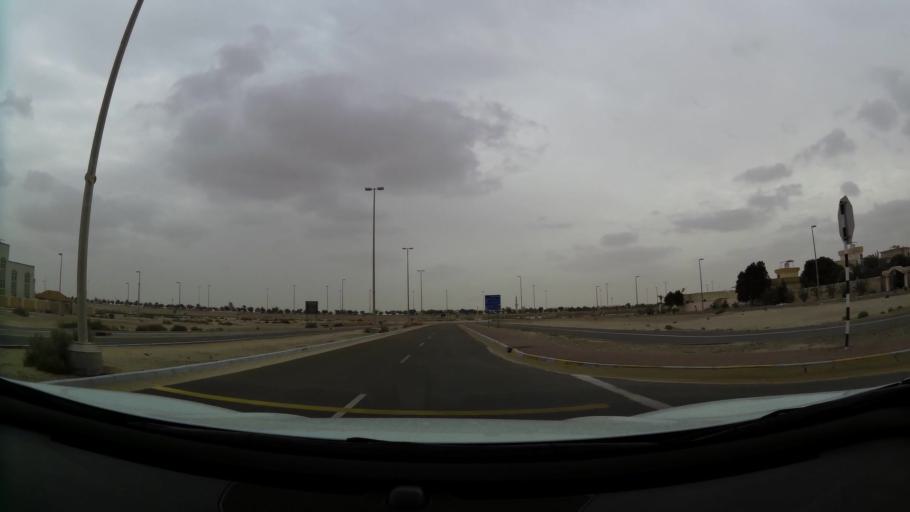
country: AE
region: Abu Dhabi
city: Abu Dhabi
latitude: 24.3801
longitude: 54.6536
